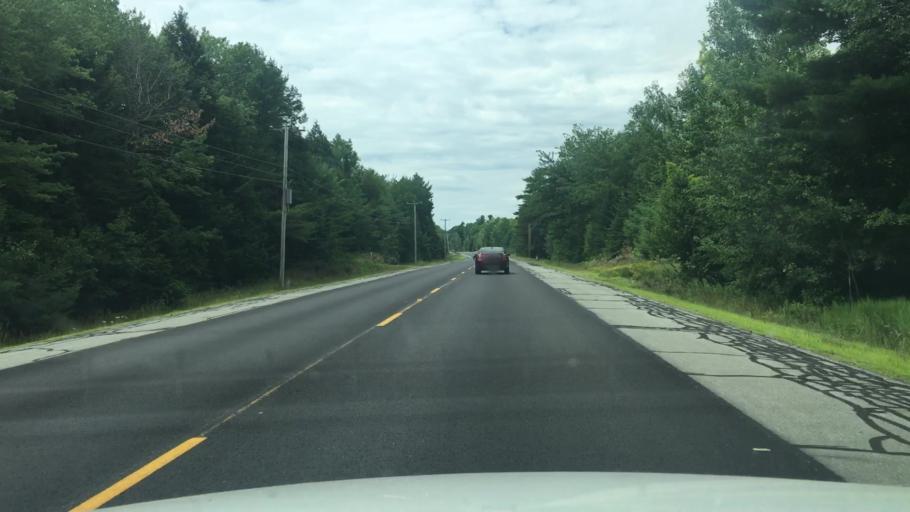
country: US
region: Maine
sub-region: Waldo County
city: Palermo
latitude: 44.4111
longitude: -69.4941
